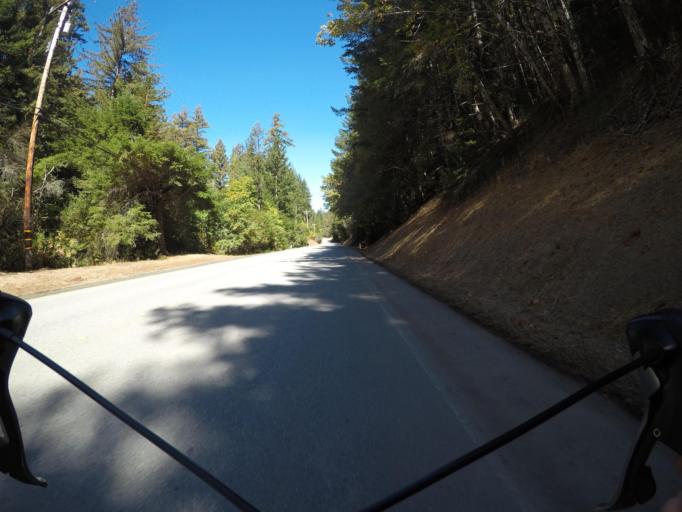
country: US
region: California
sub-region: San Mateo County
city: Portola Valley
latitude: 37.3024
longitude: -122.2669
